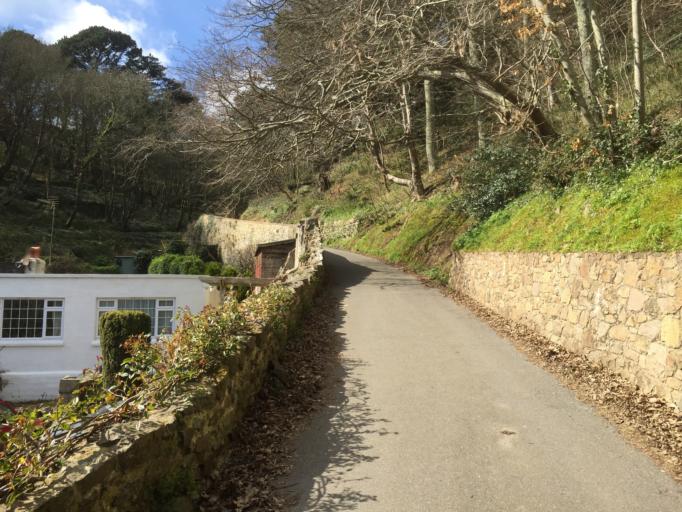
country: GG
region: St Peter Port
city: Saint Peter Port
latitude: 49.4275
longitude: -2.5499
